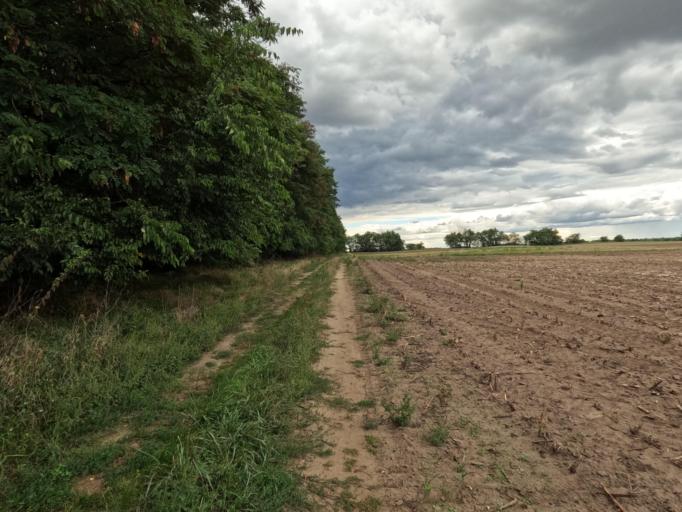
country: HU
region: Tolna
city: Tengelic
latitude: 46.5208
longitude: 18.6766
